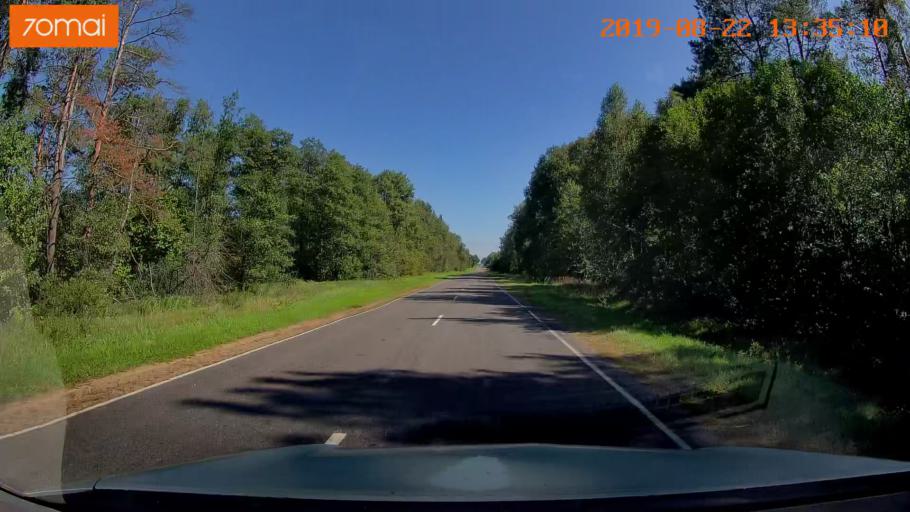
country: BY
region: Minsk
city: Staryya Darohi
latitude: 53.2141
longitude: 28.2609
